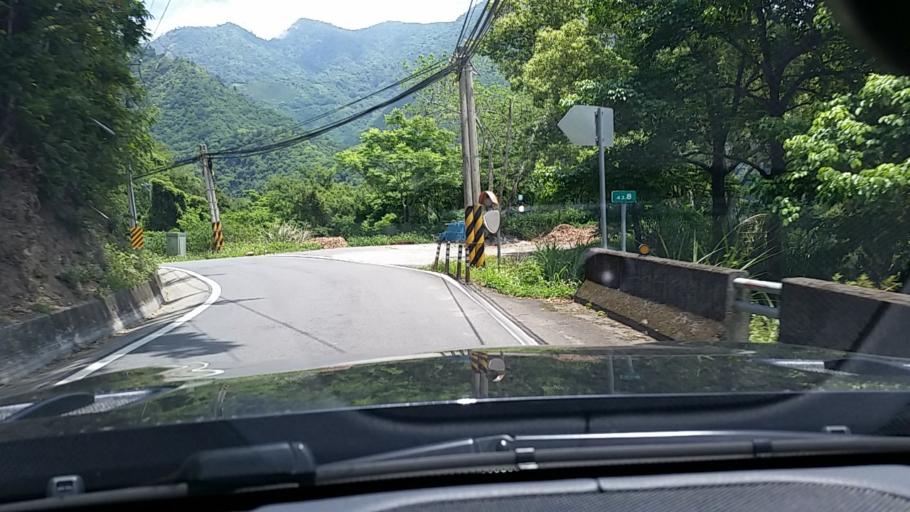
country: TW
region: Taiwan
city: Daxi
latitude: 24.6956
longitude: 121.3750
